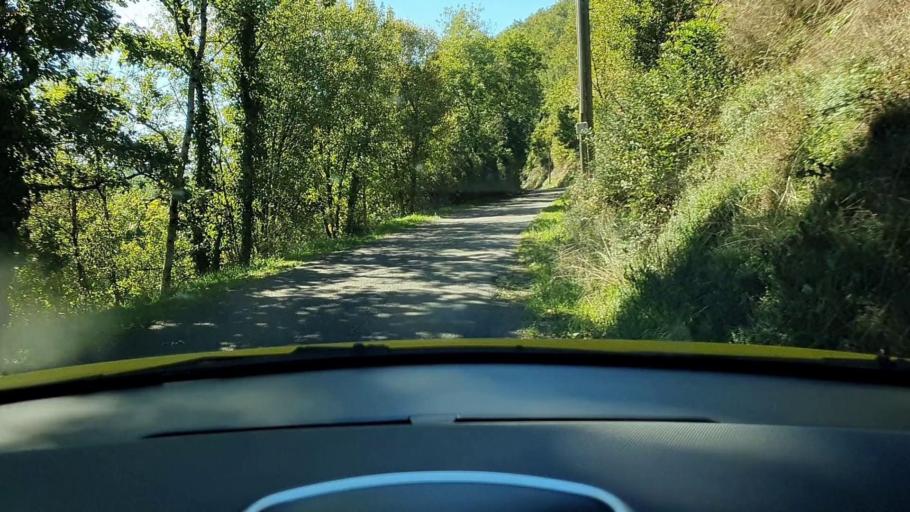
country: FR
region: Languedoc-Roussillon
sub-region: Departement du Gard
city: Le Vigan
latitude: 43.9898
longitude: 3.4519
